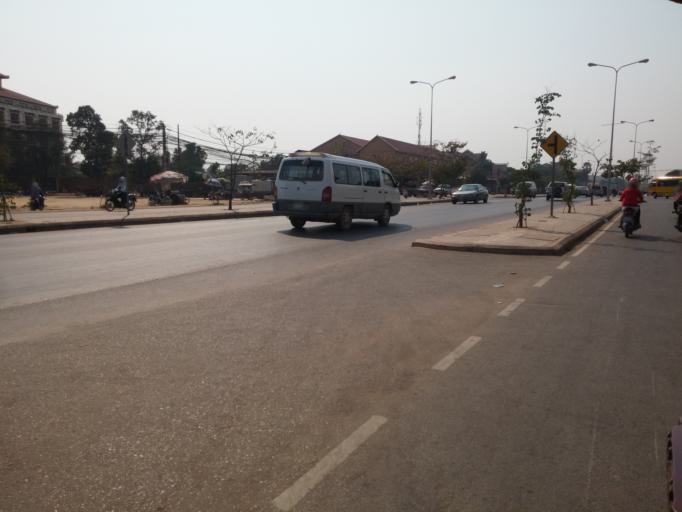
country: KH
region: Siem Reap
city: Siem Reap
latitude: 13.3671
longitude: 103.8497
